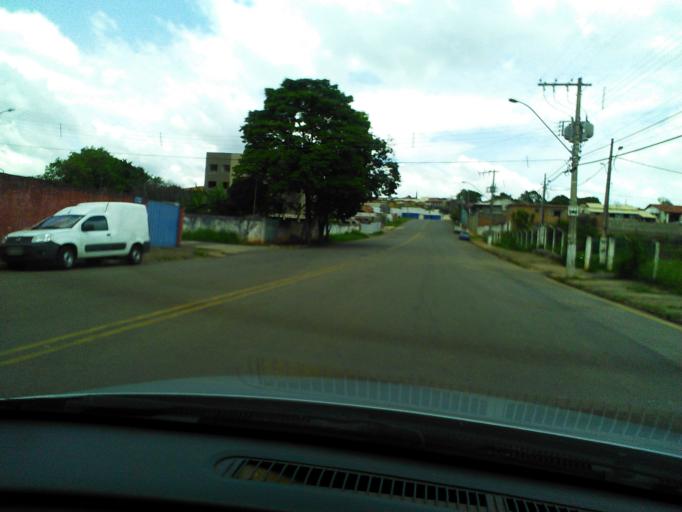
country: BR
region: Minas Gerais
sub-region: Tres Coracoes
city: Tres Coracoes
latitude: -21.6729
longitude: -45.2692
